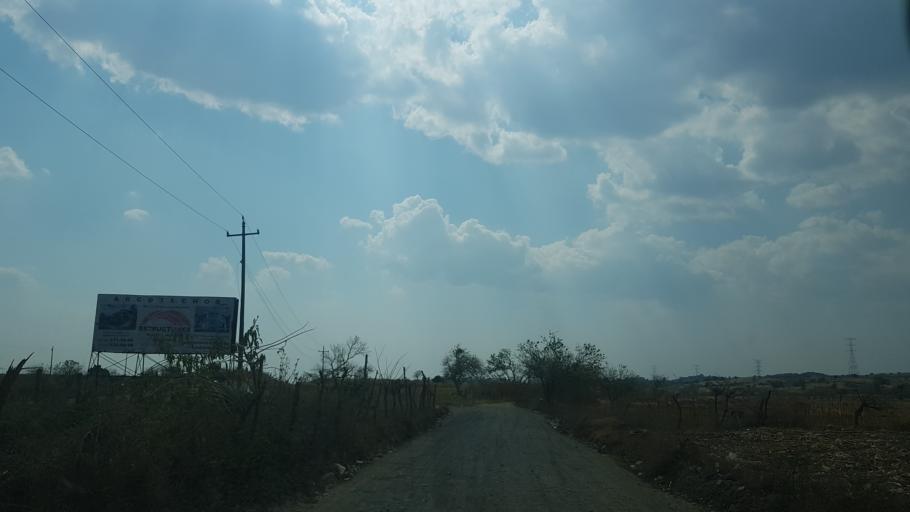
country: MX
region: Puebla
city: San Juan Amecac
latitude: 18.8174
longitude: -98.6537
